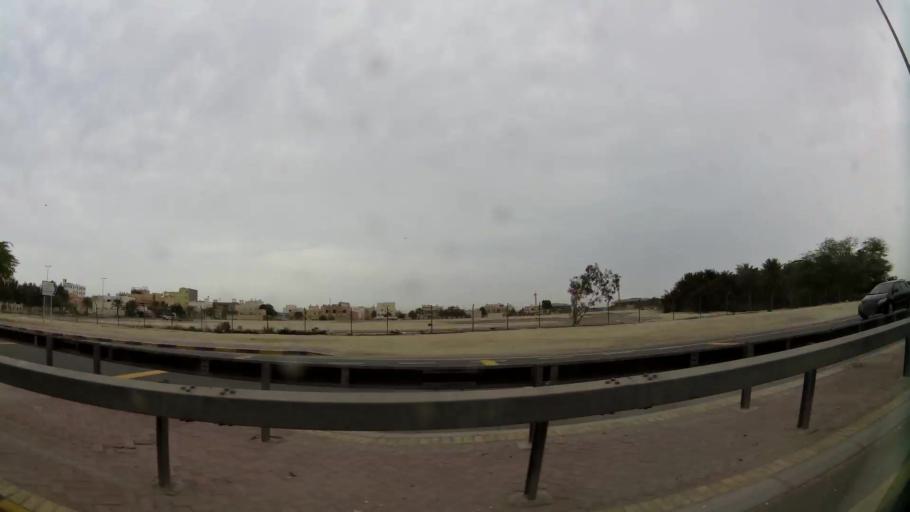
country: BH
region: Northern
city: Ar Rifa'
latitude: 26.1190
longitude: 50.5370
